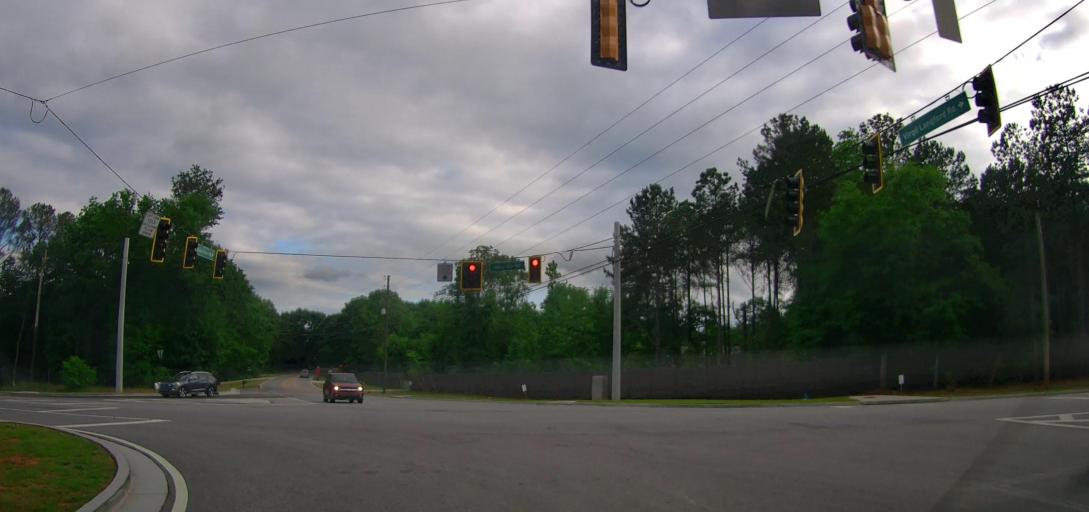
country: US
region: Georgia
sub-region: Oconee County
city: Bogart
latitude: 33.9101
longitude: -83.4752
